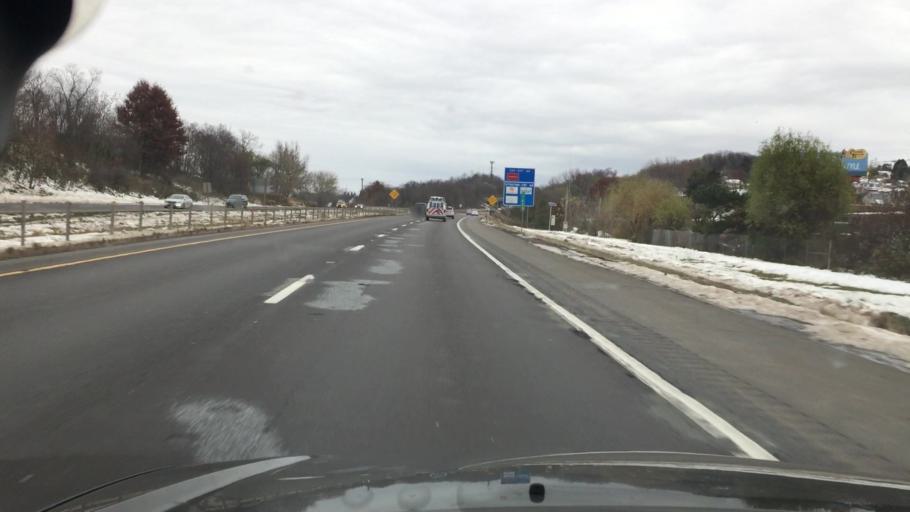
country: US
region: Pennsylvania
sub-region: Luzerne County
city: Georgetown
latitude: 41.2271
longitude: -75.8727
